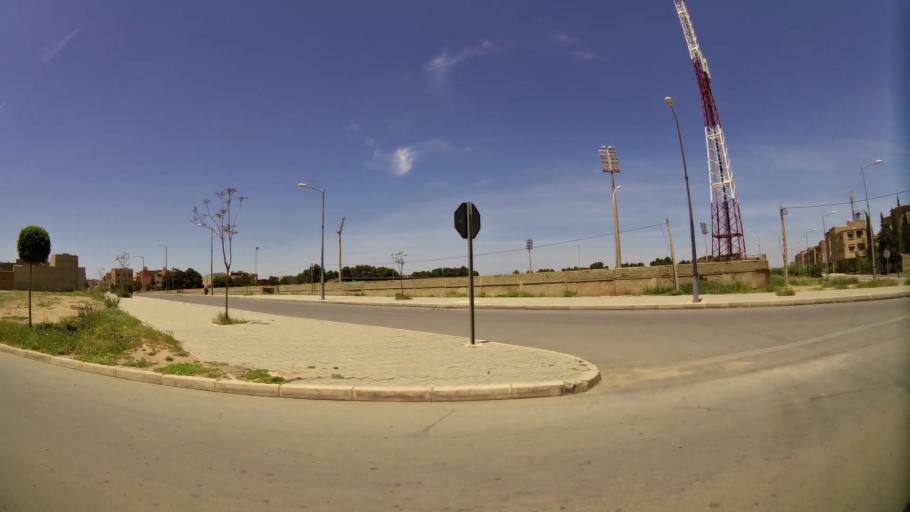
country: MA
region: Oriental
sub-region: Oujda-Angad
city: Oujda
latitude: 34.6584
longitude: -1.9330
